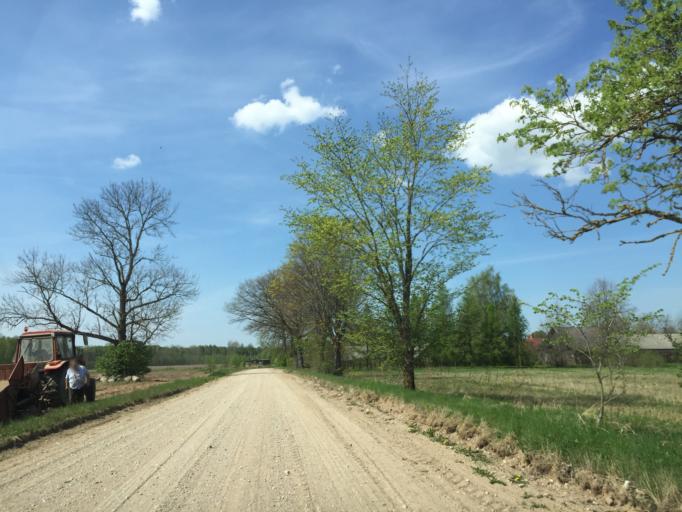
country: LV
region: Limbazu Rajons
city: Limbazi
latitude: 57.3806
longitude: 24.6199
